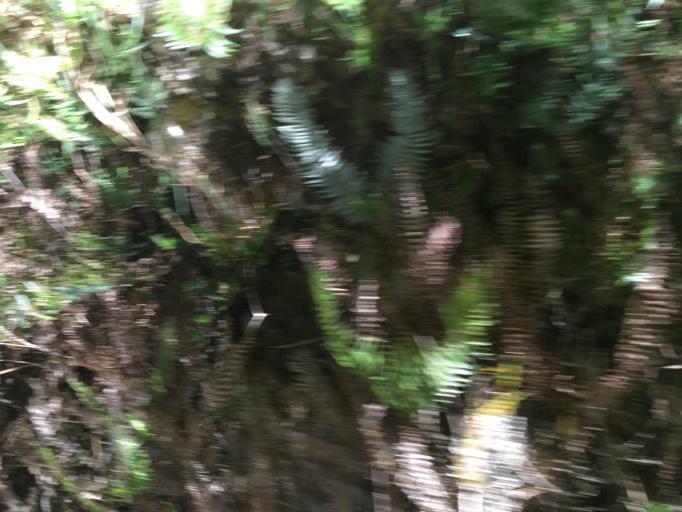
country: TW
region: Taiwan
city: Daxi
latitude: 24.5357
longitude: 121.4018
